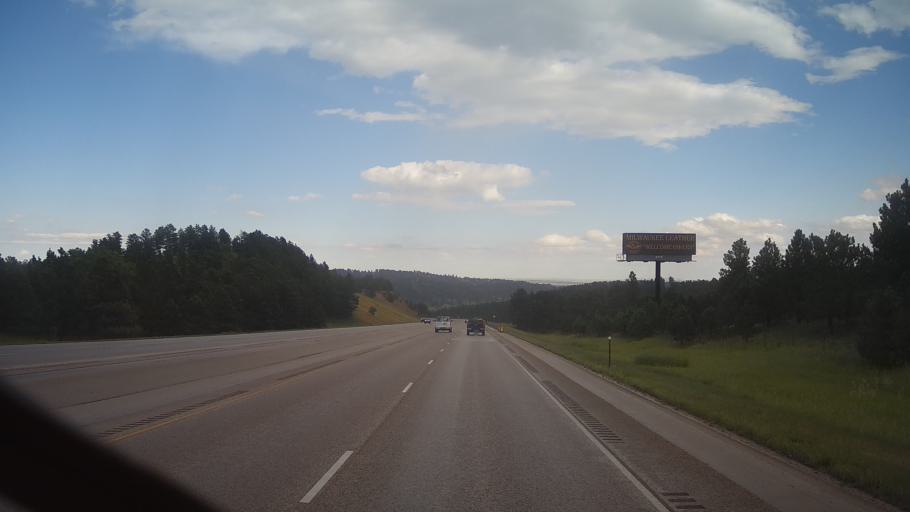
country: US
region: South Dakota
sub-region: Pennington County
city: Colonial Pine Hills
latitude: 43.9740
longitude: -103.2910
